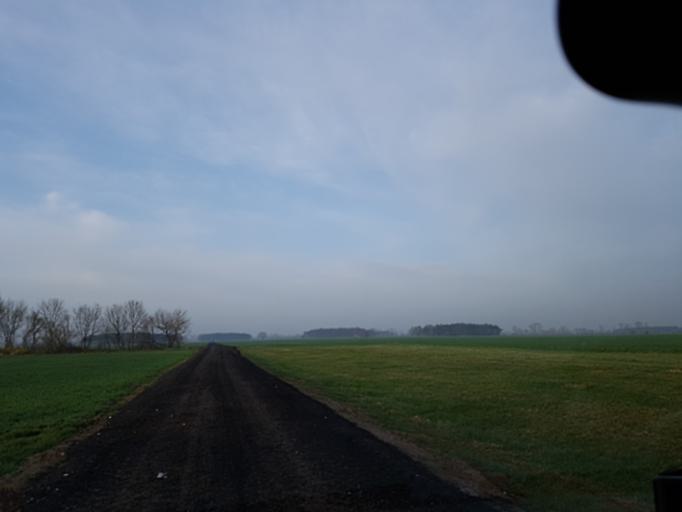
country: DE
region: Brandenburg
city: Falkenberg
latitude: 51.5248
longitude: 13.2909
